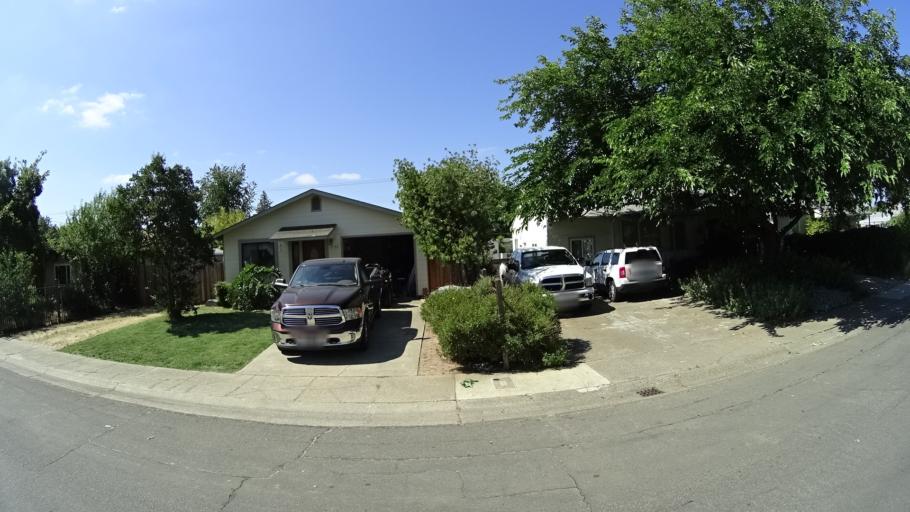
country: US
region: California
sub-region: Sacramento County
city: Sacramento
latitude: 38.5346
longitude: -121.4881
